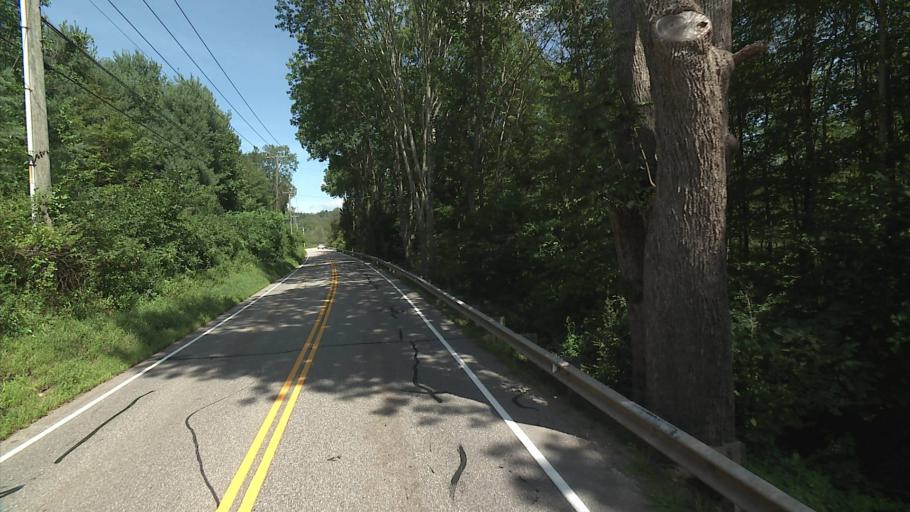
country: US
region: Connecticut
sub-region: Windham County
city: South Woodstock
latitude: 41.8970
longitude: -72.0790
